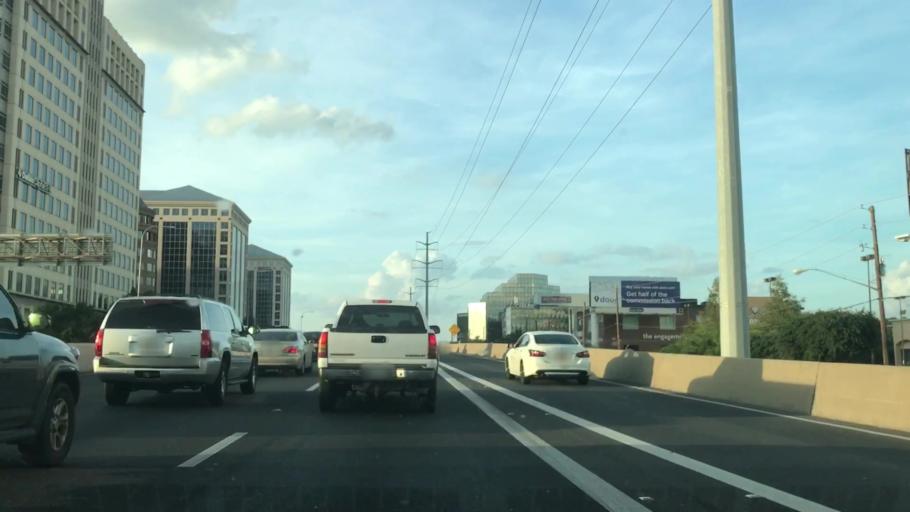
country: US
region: Texas
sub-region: Dallas County
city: Addison
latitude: 32.9379
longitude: -96.8219
